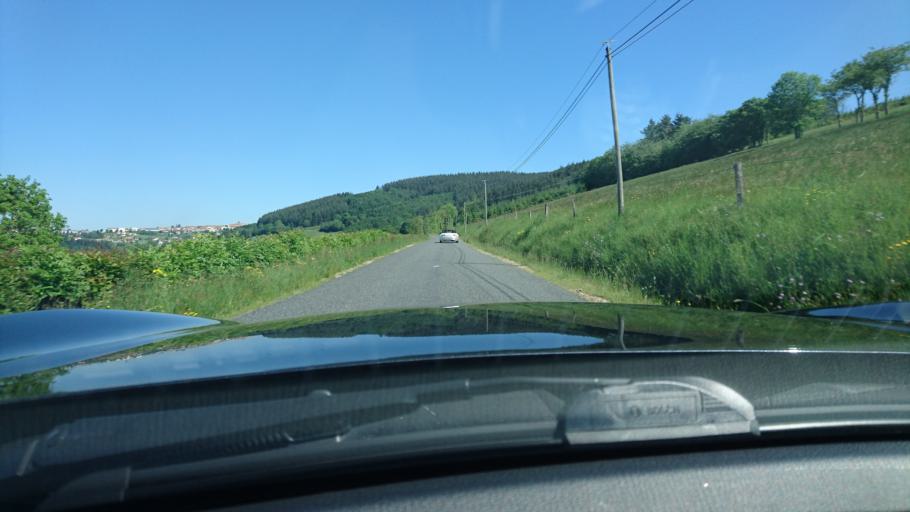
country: FR
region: Rhone-Alpes
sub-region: Departement de la Loire
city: Violay
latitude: 45.8338
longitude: 4.3708
